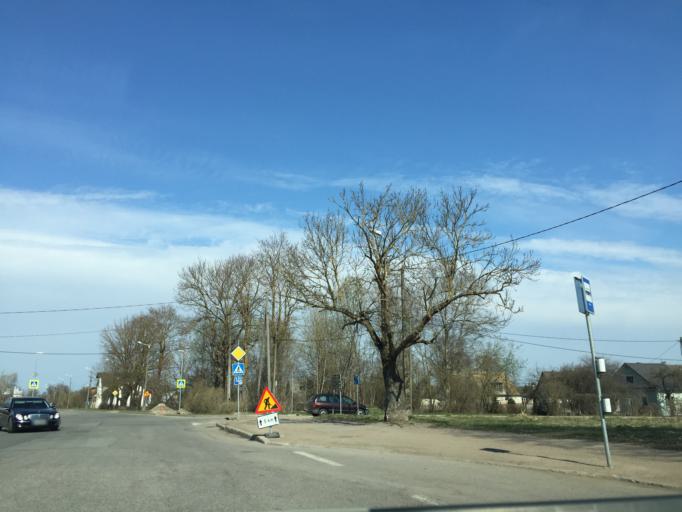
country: EE
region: Ida-Virumaa
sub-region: Narva linn
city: Narva
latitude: 59.3862
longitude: 28.1984
